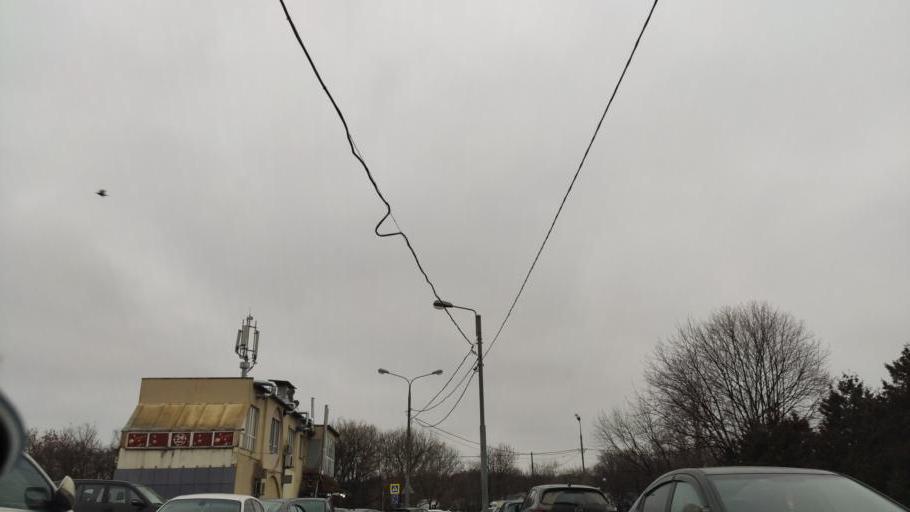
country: RU
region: Moscow
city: Orekhovo-Borisovo Severnoye
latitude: 55.6128
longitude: 37.6964
